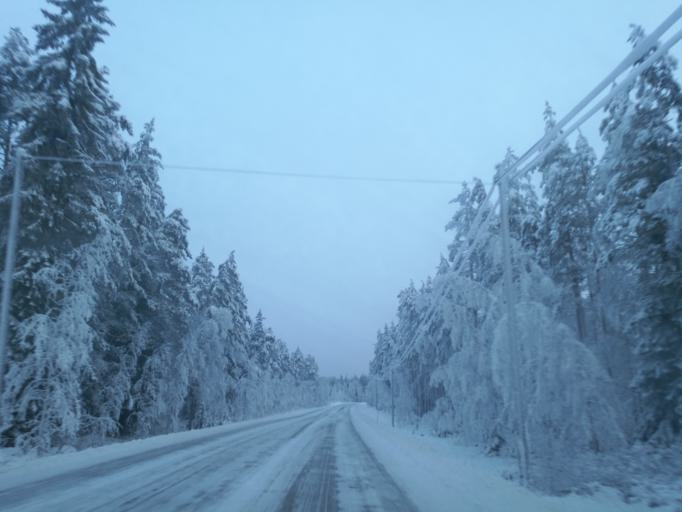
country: NO
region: Hedmark
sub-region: Grue
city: Kirkenaer
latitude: 60.3992
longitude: 12.3712
